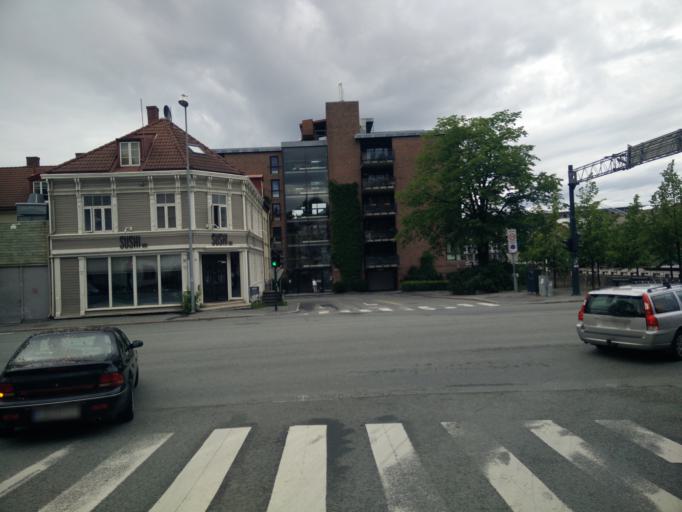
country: NO
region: Sor-Trondelag
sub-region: Trondheim
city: Trondheim
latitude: 63.4331
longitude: 10.4113
